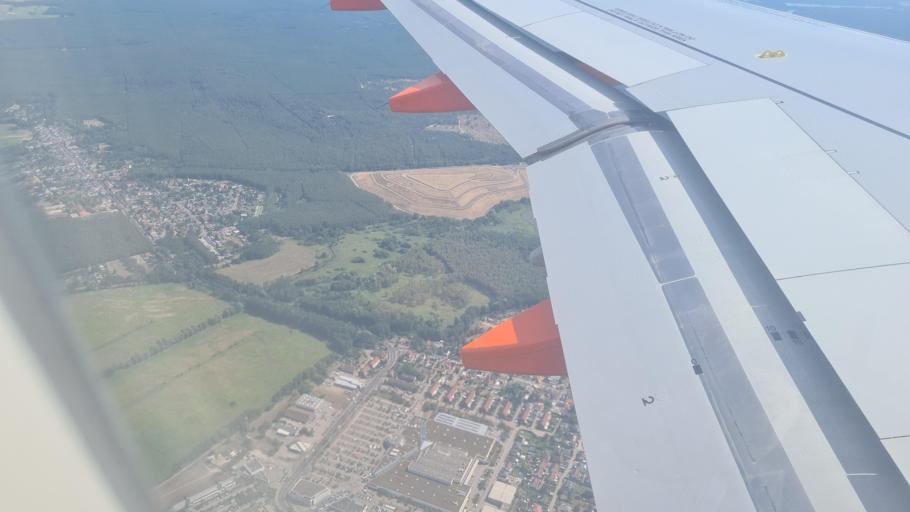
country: DE
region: Brandenburg
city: Erkner
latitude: 52.4030
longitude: 13.7127
